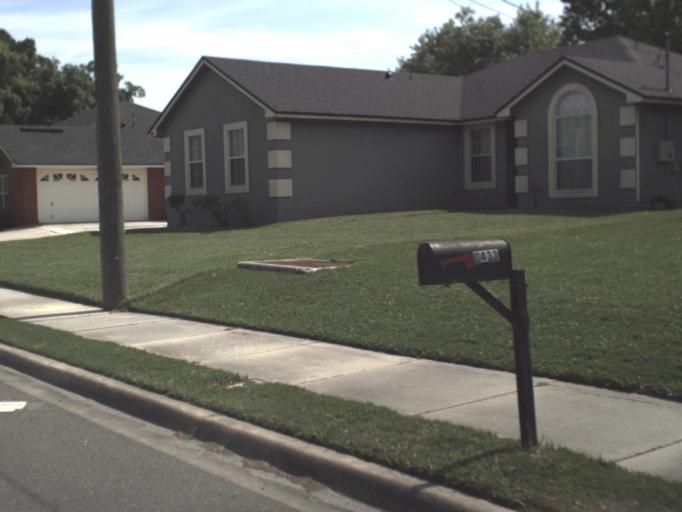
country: US
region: Florida
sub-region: Duval County
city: Jacksonville
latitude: 30.3021
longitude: -81.6010
